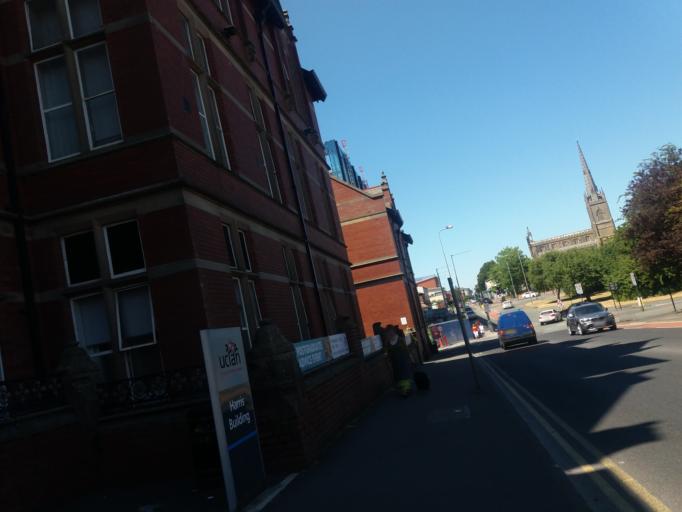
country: GB
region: England
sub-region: Lancashire
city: Preston
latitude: 53.7615
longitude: -2.7070
